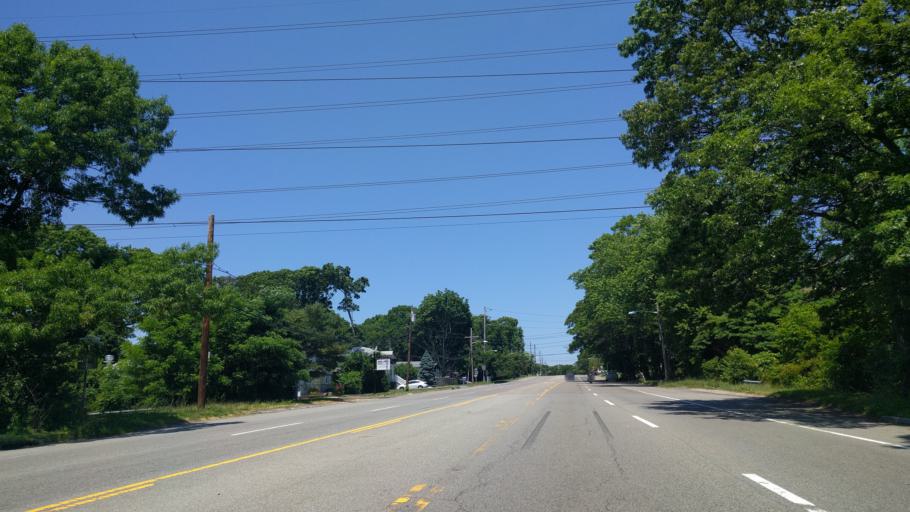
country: US
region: New York
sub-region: Suffolk County
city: Ronkonkoma
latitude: 40.8138
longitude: -73.1252
